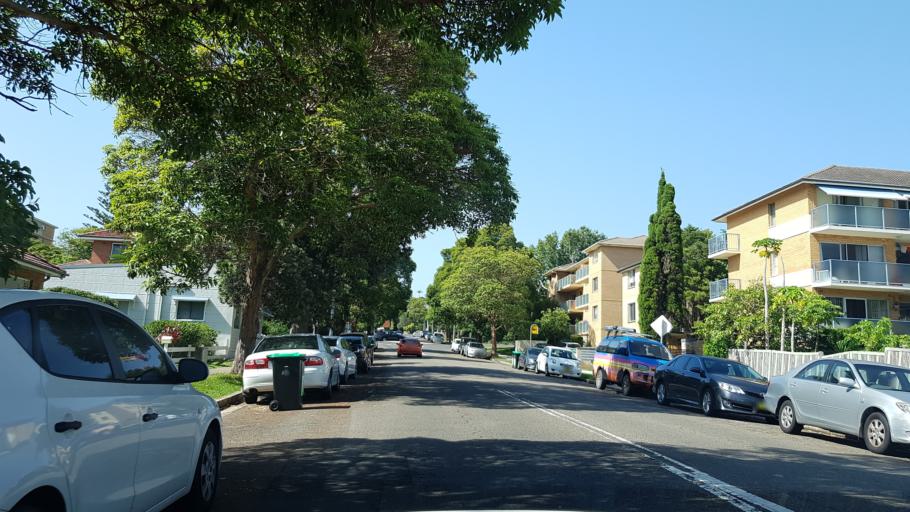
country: AU
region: New South Wales
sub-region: Warringah
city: Dee Why
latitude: -33.7533
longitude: 151.2922
